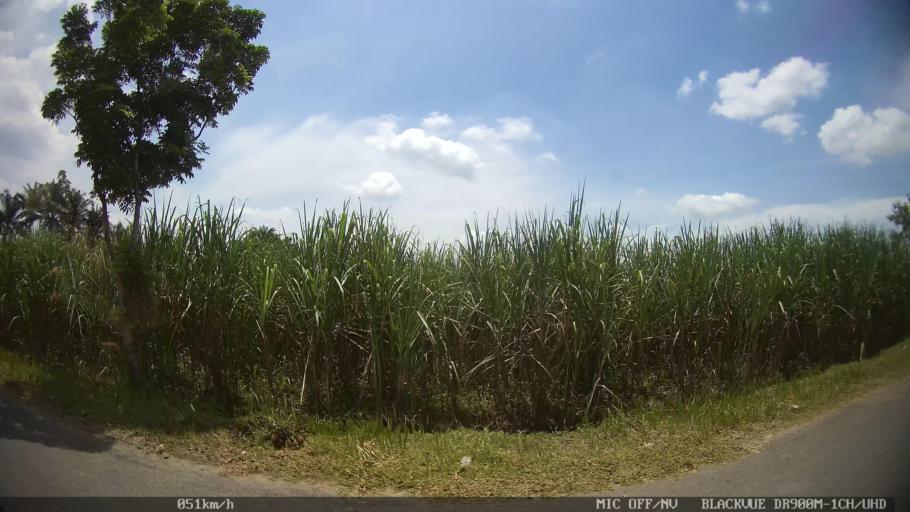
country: ID
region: North Sumatra
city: Binjai
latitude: 3.5923
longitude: 98.5329
